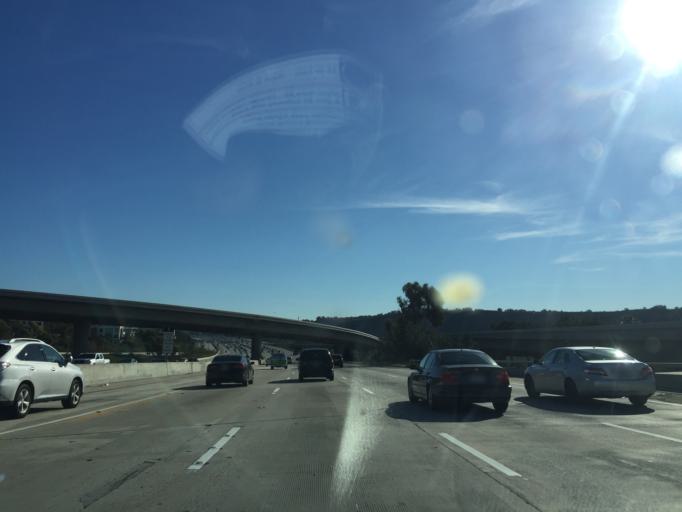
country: US
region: California
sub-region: San Diego County
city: Del Mar
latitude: 32.9329
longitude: -117.2414
